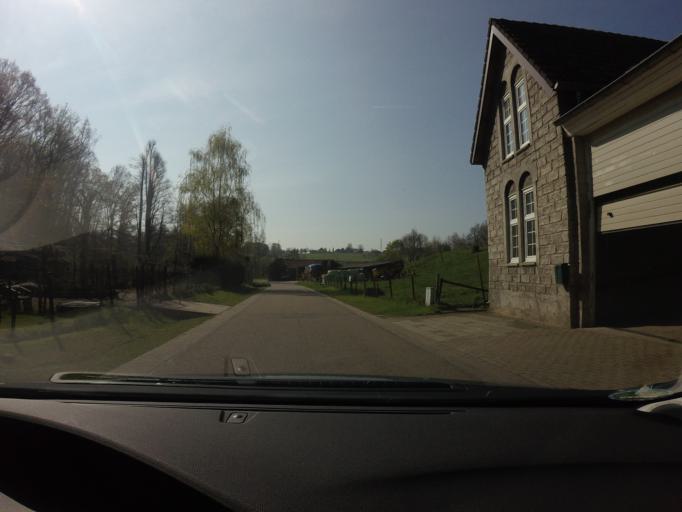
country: NL
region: Limburg
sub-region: Valkenburg aan de Geul
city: Houthem
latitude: 50.8937
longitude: 5.7770
